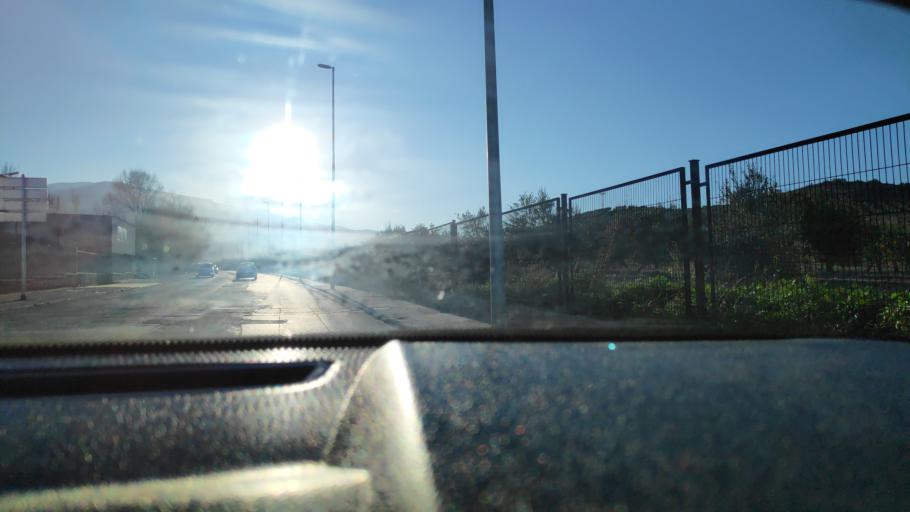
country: ES
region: Andalusia
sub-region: Provincia de Jaen
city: Jaen
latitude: 37.8019
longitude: -3.7886
